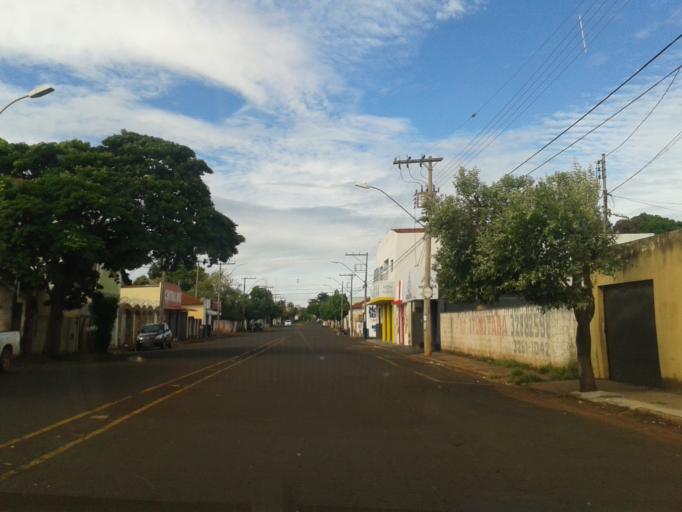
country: BR
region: Minas Gerais
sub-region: Ituiutaba
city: Ituiutaba
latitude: -18.9773
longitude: -49.4674
